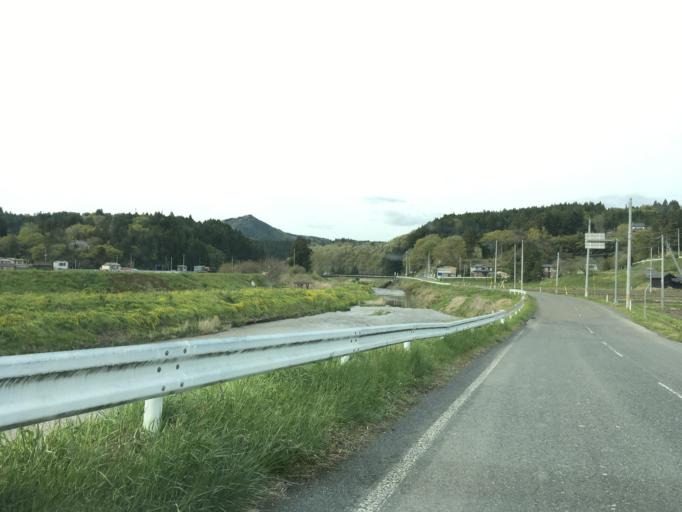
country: JP
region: Iwate
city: Ichinoseki
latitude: 38.8467
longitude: 141.3018
